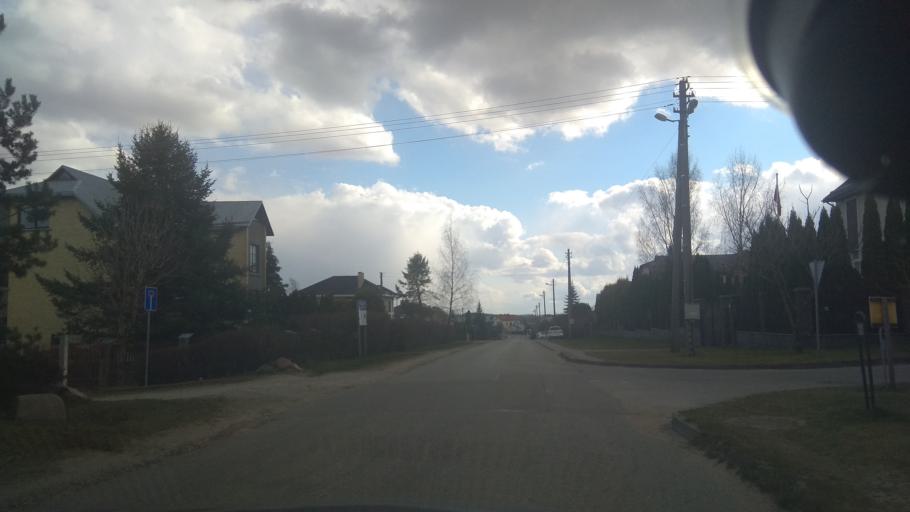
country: LT
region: Vilnius County
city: Pasilaiciai
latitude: 54.7386
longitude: 25.2021
